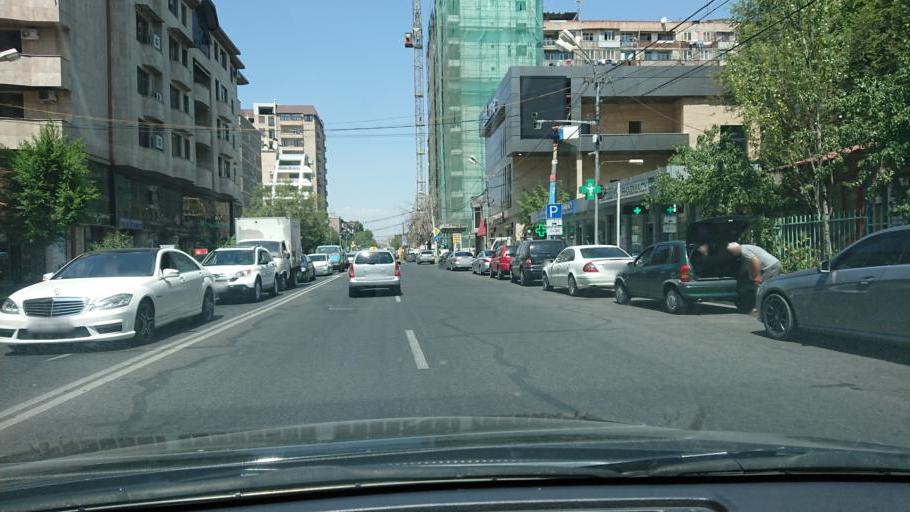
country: AM
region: Yerevan
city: Yerevan
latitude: 40.1990
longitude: 44.5014
